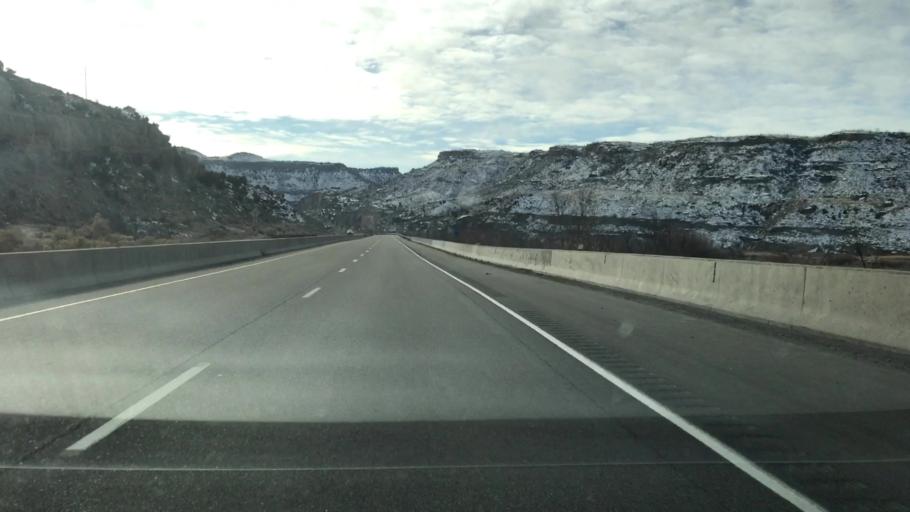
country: US
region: Colorado
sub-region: Mesa County
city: Palisade
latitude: 39.2591
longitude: -108.2595
